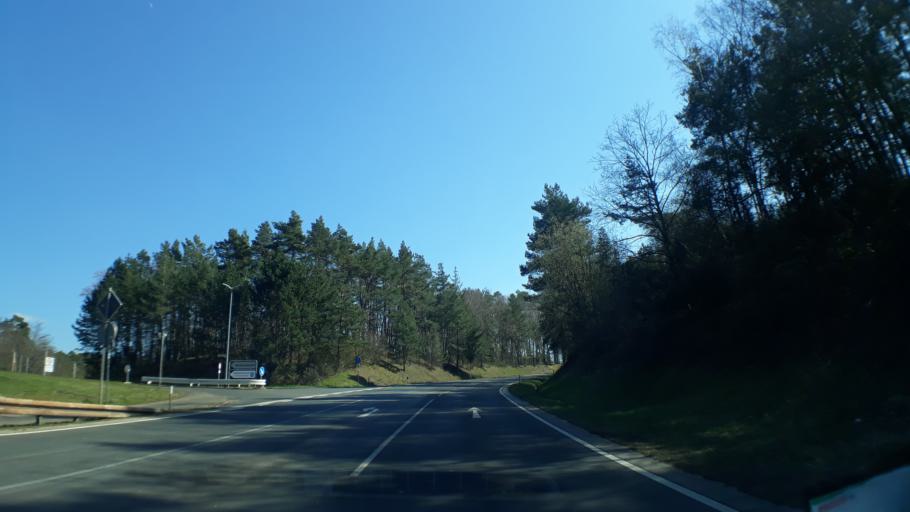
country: DE
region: North Rhine-Westphalia
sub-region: Regierungsbezirk Koln
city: Mechernich
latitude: 50.5838
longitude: 6.6520
